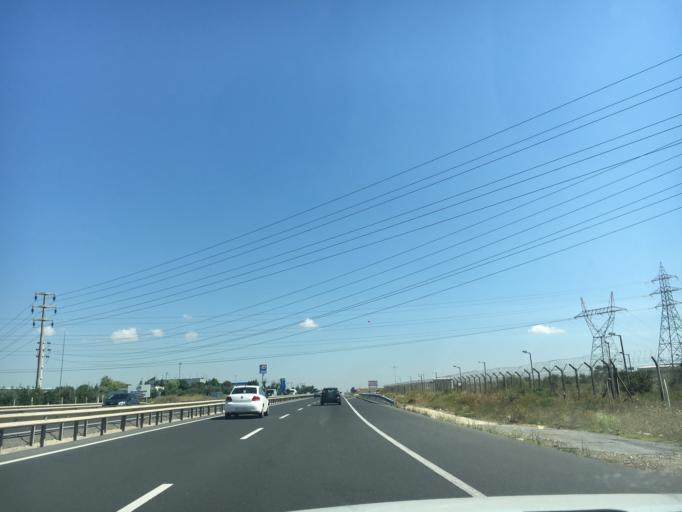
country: TR
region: Tekirdag
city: Marmara Ereglisi
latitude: 40.9944
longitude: 27.9729
